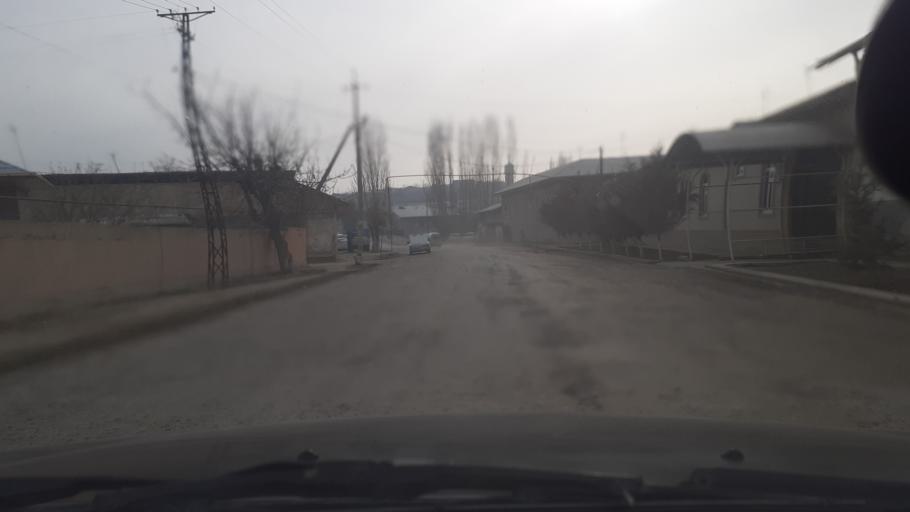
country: UZ
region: Namangan
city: Namangan
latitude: 41.0445
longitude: 71.6741
